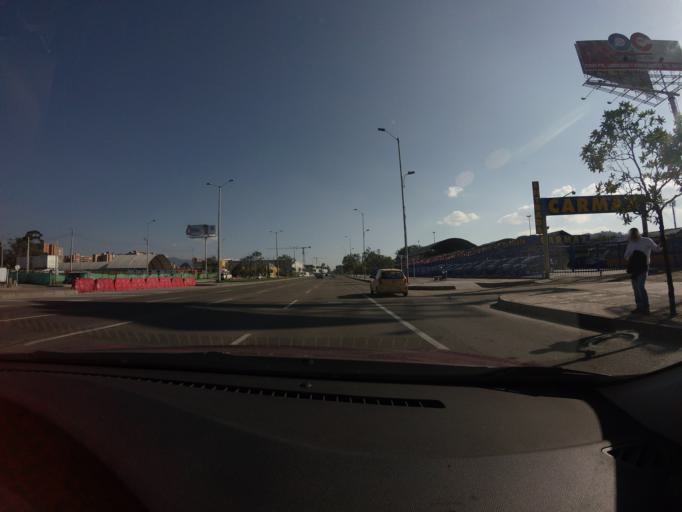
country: CO
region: Cundinamarca
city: Cota
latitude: 4.7370
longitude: -74.0664
